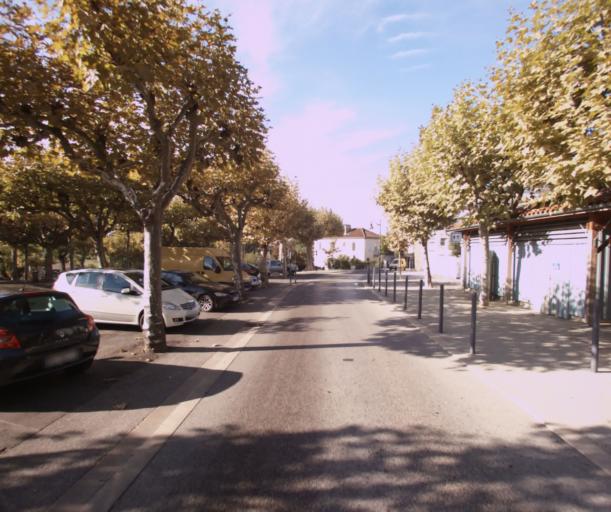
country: FR
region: Midi-Pyrenees
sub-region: Departement du Gers
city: Eauze
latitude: 43.8607
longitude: 0.0988
